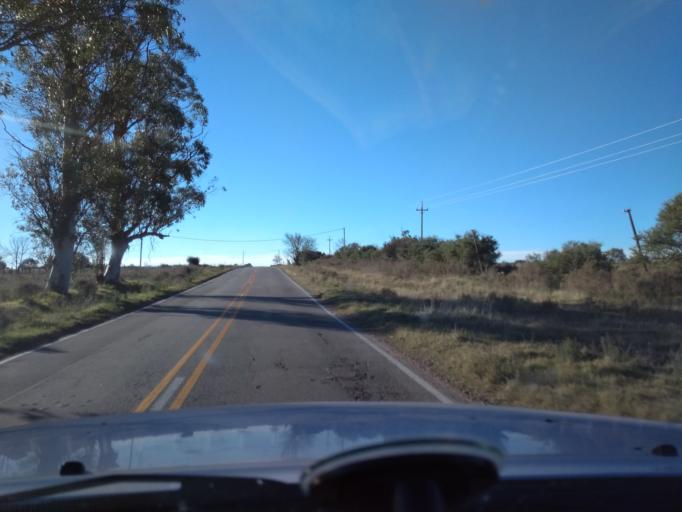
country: UY
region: Canelones
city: San Ramon
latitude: -34.3449
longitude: -55.9597
